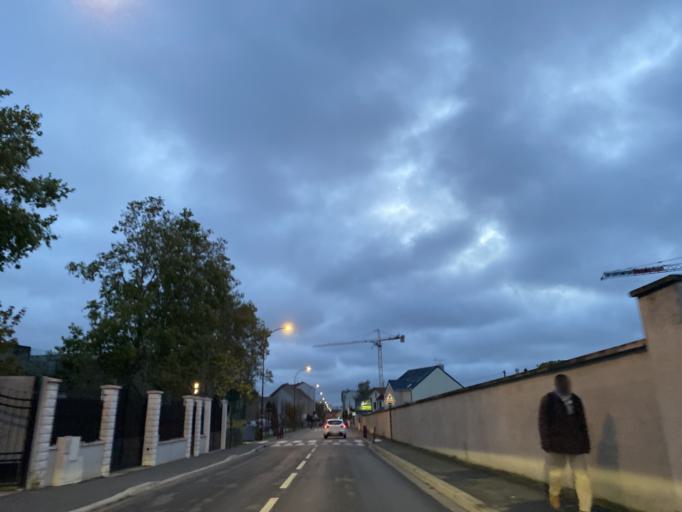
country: FR
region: Ile-de-France
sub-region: Departement du Val-d'Oise
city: Bezons
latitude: 48.9277
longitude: 2.2187
